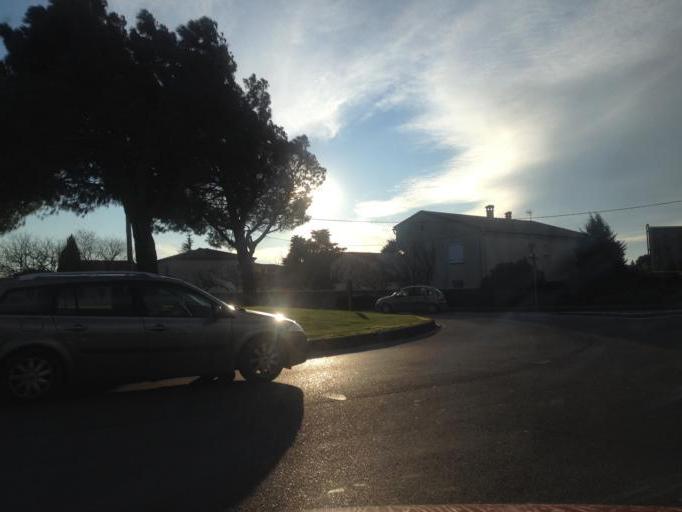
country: FR
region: Provence-Alpes-Cote d'Azur
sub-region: Departement du Vaucluse
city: Orange
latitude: 44.1516
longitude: 4.8062
